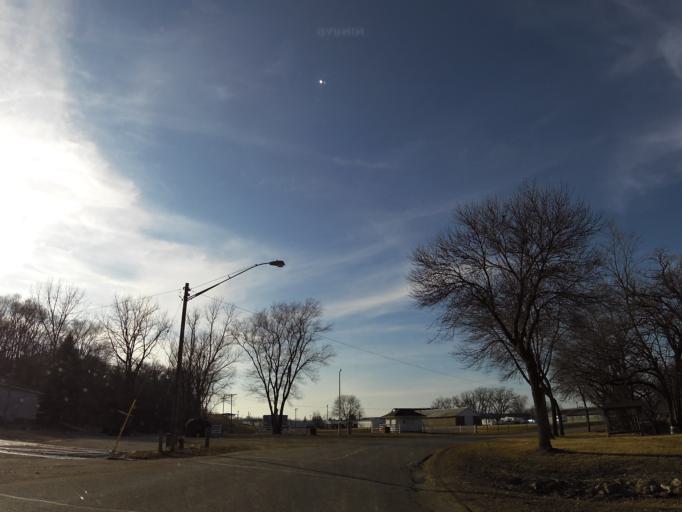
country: US
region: Minnesota
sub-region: Goodhue County
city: Cannon Falls
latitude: 44.5132
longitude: -92.9116
